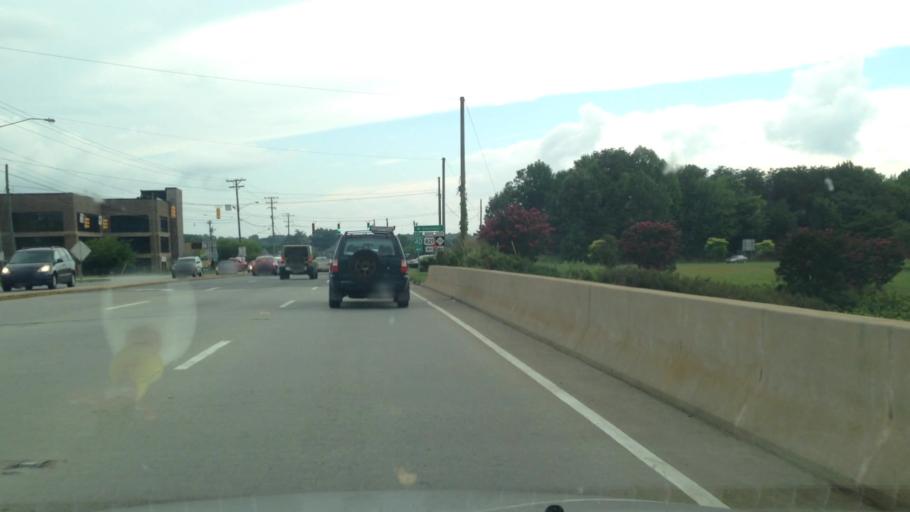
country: US
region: North Carolina
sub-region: Forsyth County
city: Kernersville
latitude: 36.1103
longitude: -80.0915
